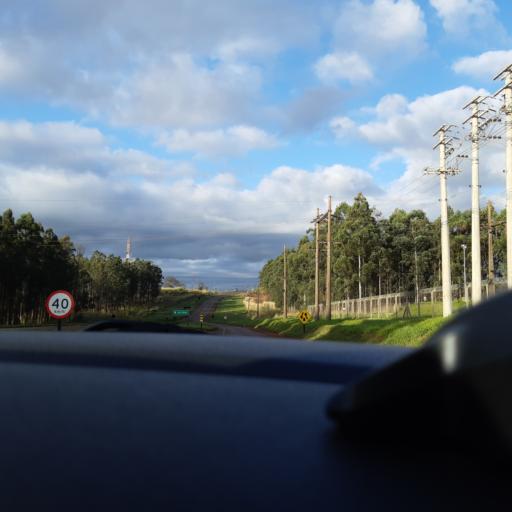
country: BR
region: Sao Paulo
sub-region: Ourinhos
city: Ourinhos
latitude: -22.9958
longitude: -49.8519
